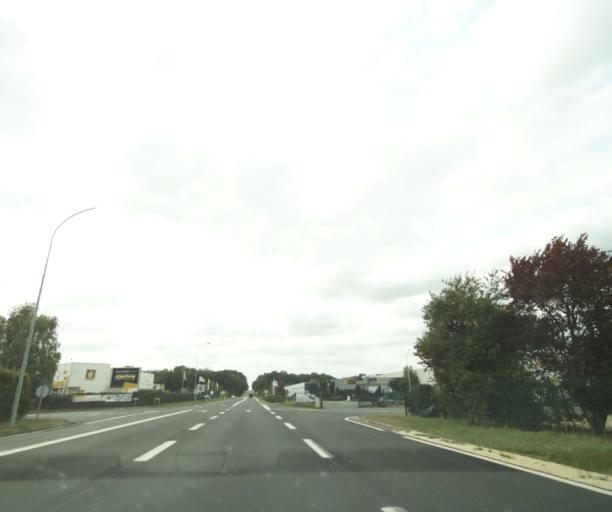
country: FR
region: Centre
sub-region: Departement de l'Indre
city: Buzancais
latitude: 46.8919
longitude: 1.3980
